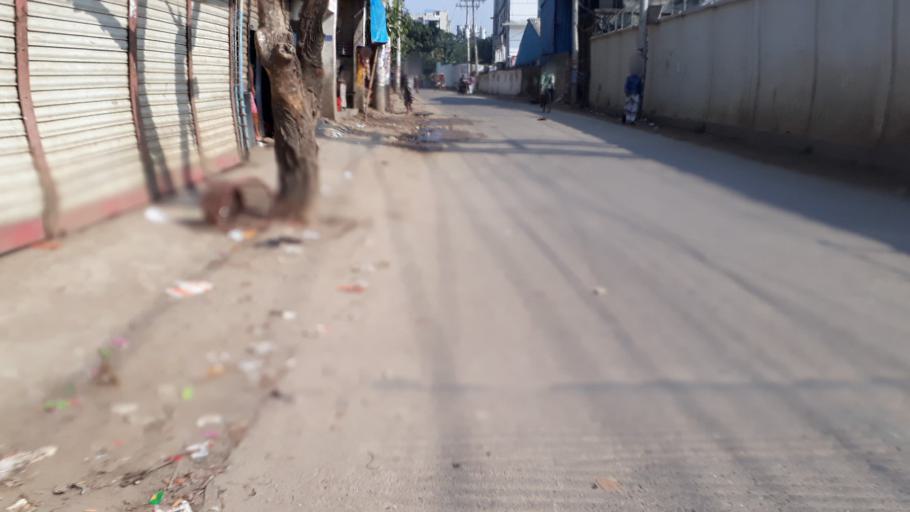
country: BD
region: Dhaka
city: Tungi
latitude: 23.8903
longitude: 90.3234
